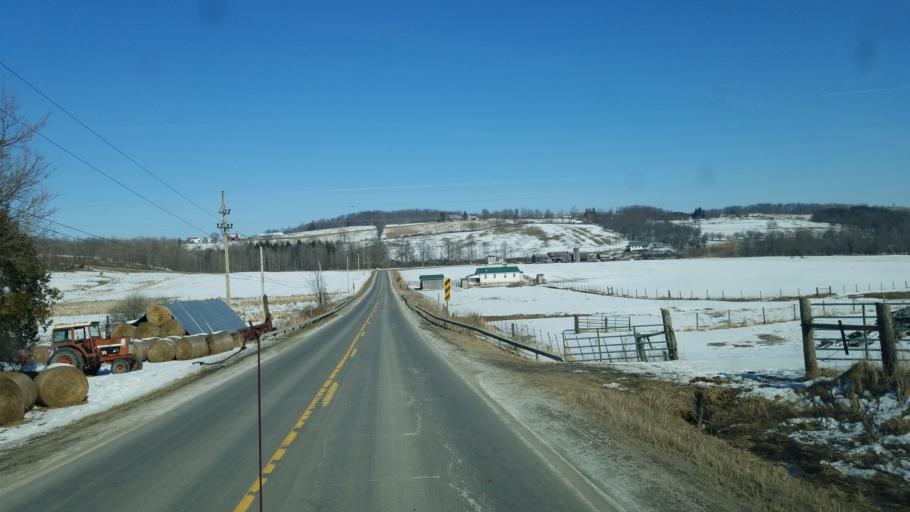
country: US
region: Pennsylvania
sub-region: Tioga County
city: Elkland
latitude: 42.0708
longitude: -77.4301
